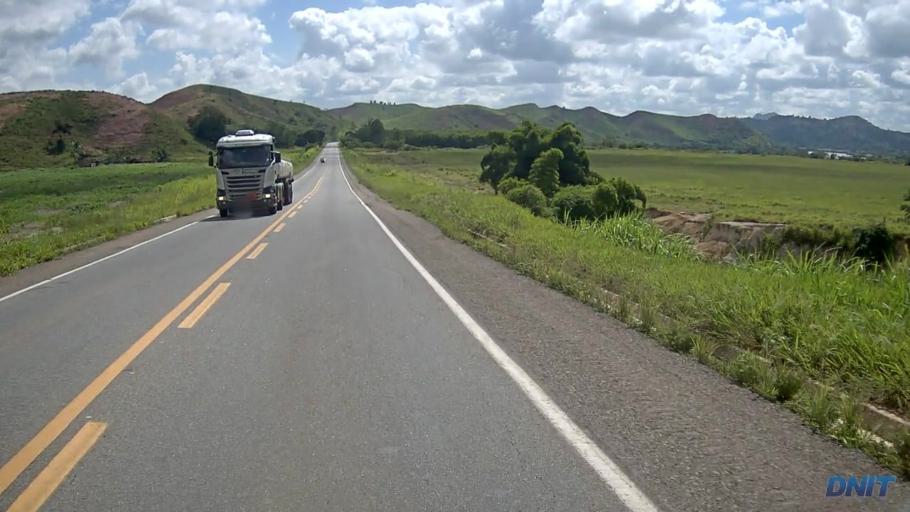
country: BR
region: Minas Gerais
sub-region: Belo Oriente
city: Belo Oriente
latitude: -19.1434
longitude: -42.2266
